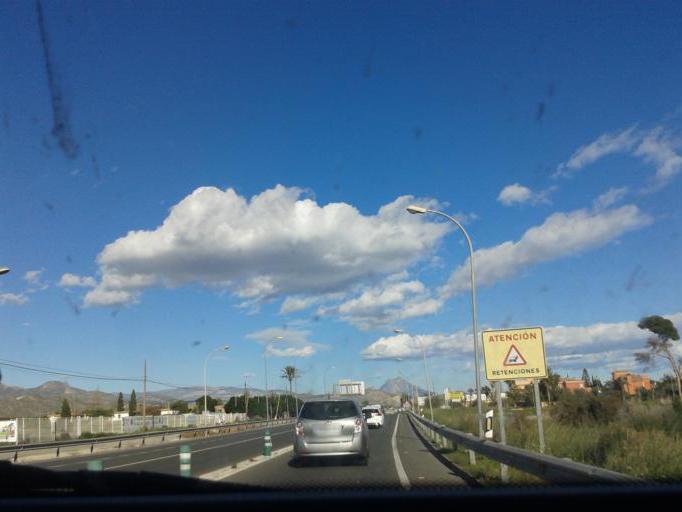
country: ES
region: Valencia
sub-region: Provincia de Alicante
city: San Juan de Alicante
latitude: 38.4148
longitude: -0.4186
